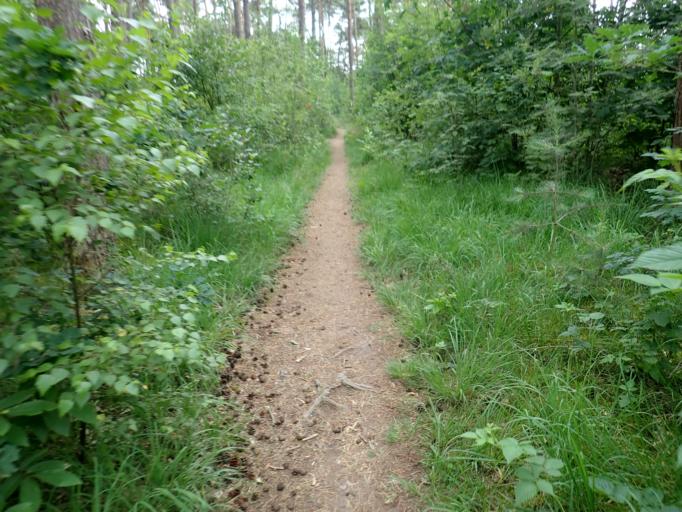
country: BE
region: Flanders
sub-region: Provincie Antwerpen
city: Bonheiden
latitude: 51.0176
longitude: 4.5862
